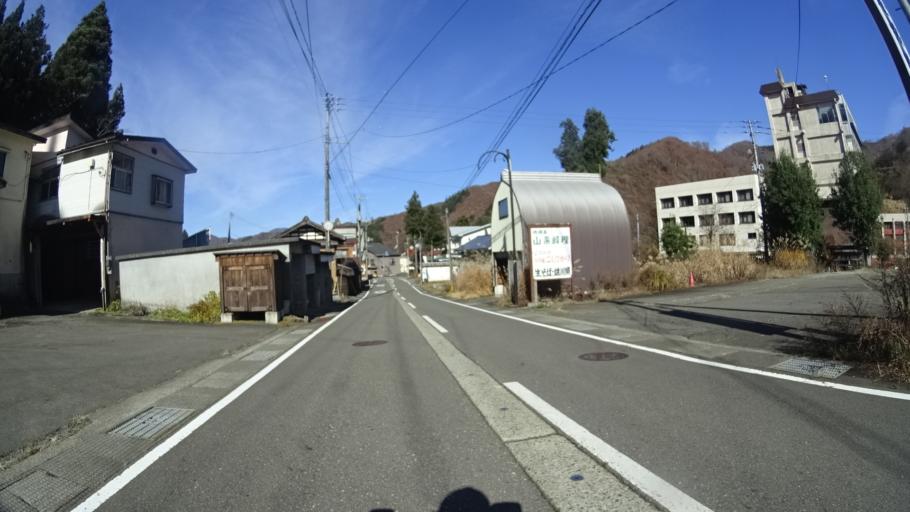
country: JP
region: Niigata
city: Muikamachi
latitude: 37.1920
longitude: 139.0806
